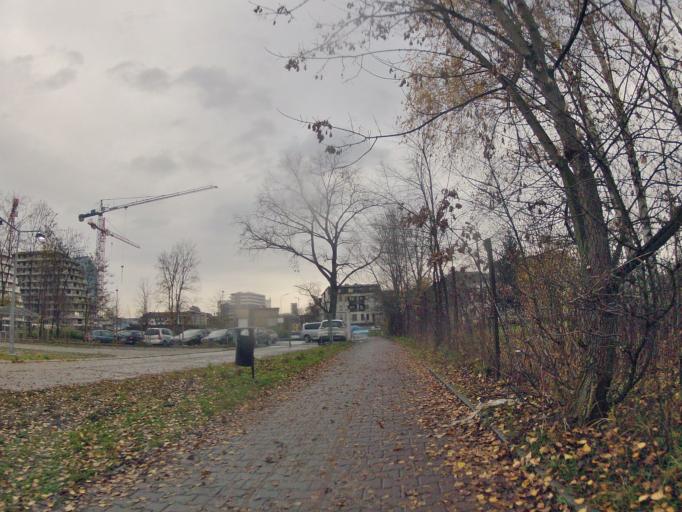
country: PL
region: Lesser Poland Voivodeship
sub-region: Krakow
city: Krakow
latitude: 50.0546
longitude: 19.9656
